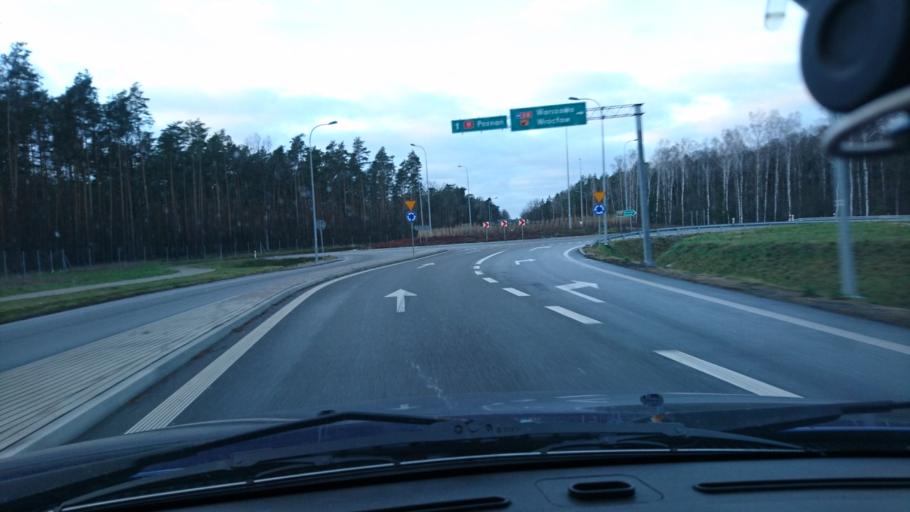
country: PL
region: Greater Poland Voivodeship
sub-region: Powiat kepinski
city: Kepno
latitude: 51.3306
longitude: 17.9592
